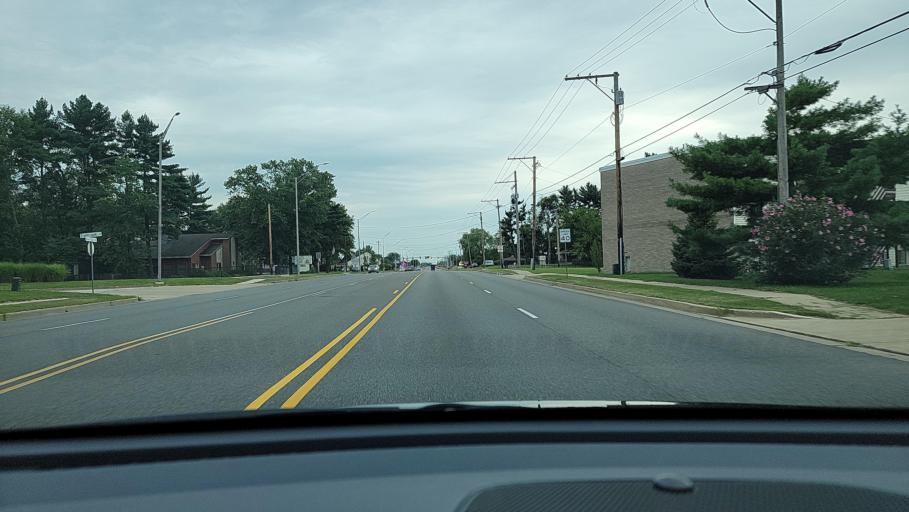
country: US
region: Indiana
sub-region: Porter County
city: Portage
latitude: 41.5644
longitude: -87.1829
